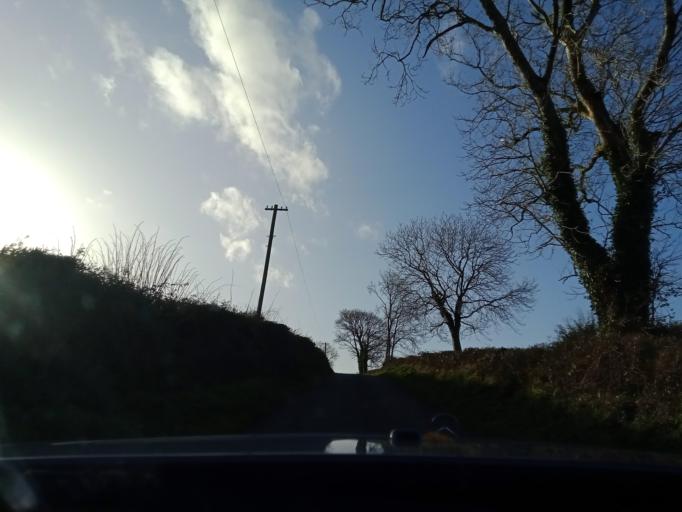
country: IE
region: Leinster
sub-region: Kilkenny
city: Callan
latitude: 52.4960
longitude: -7.3921
